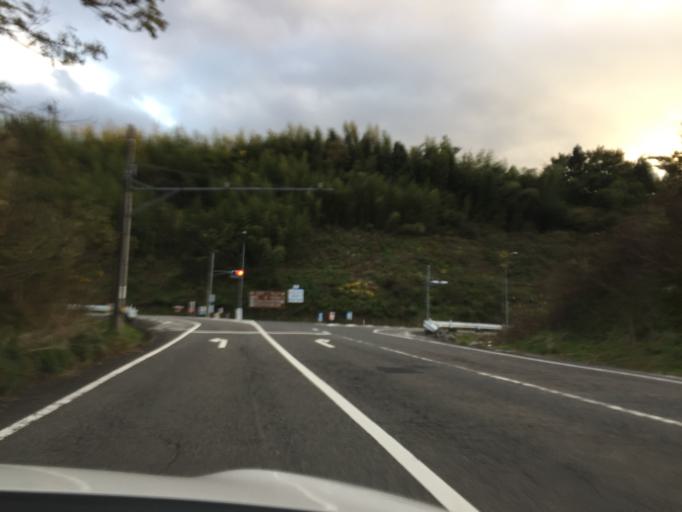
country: JP
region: Fukushima
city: Miharu
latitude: 37.4362
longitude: 140.4374
